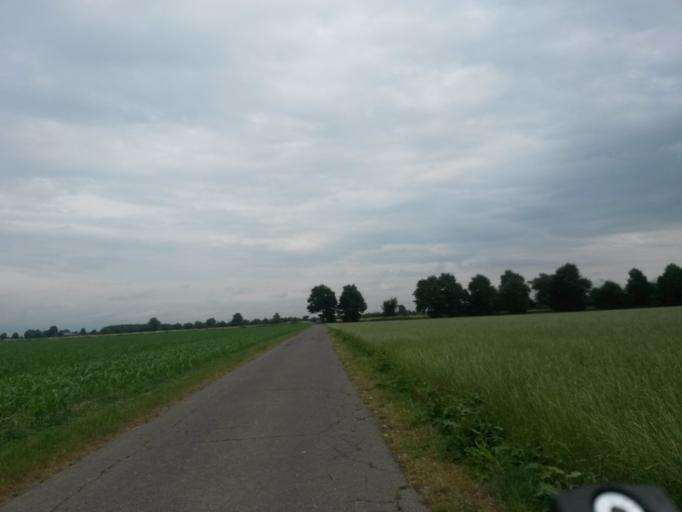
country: DE
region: North Rhine-Westphalia
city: Kempen
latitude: 51.3560
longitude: 6.4493
